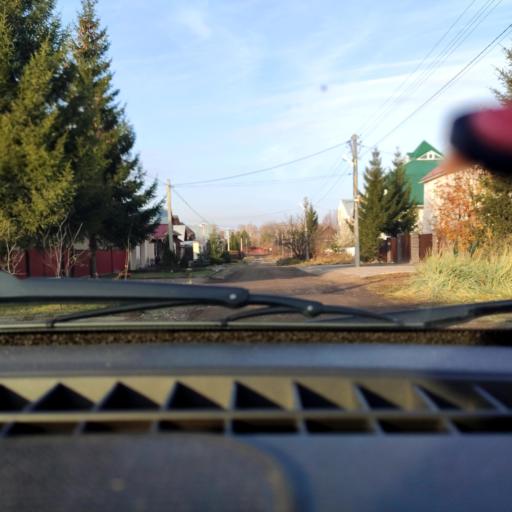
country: RU
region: Bashkortostan
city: Ufa
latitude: 54.6077
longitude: 55.9272
